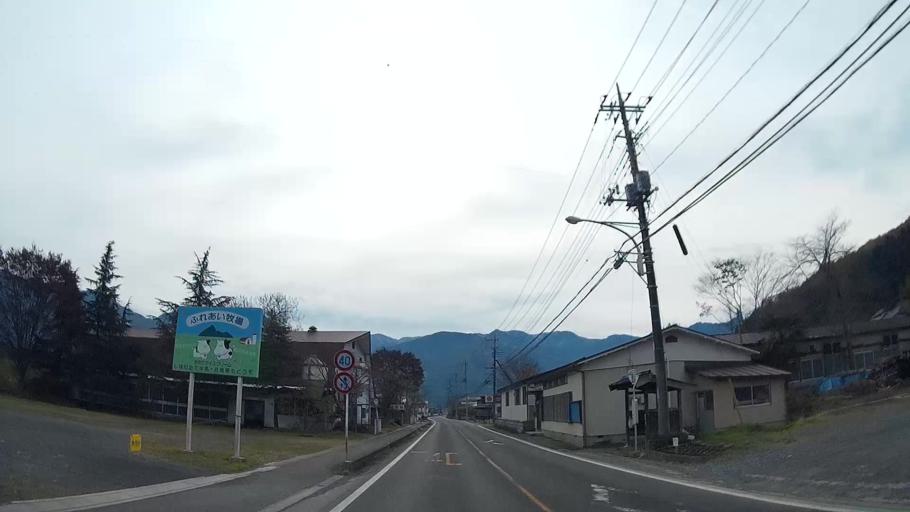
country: JP
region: Saitama
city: Chichibu
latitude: 35.9763
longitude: 139.0538
